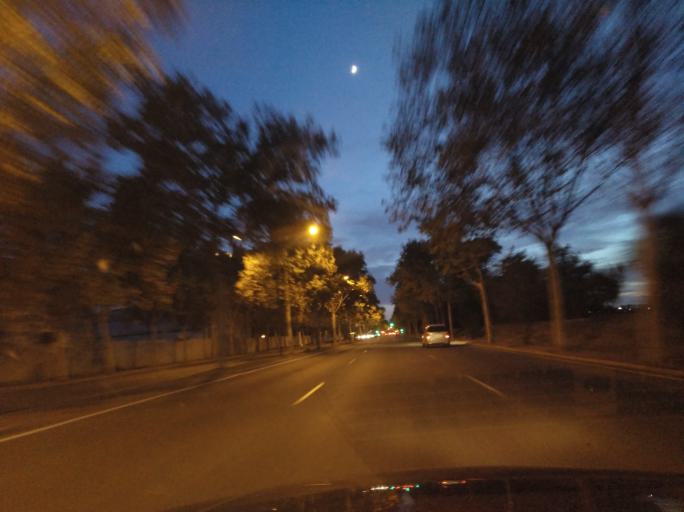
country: ES
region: Andalusia
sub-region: Provincia de Sevilla
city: Camas
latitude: 37.4005
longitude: -6.0114
